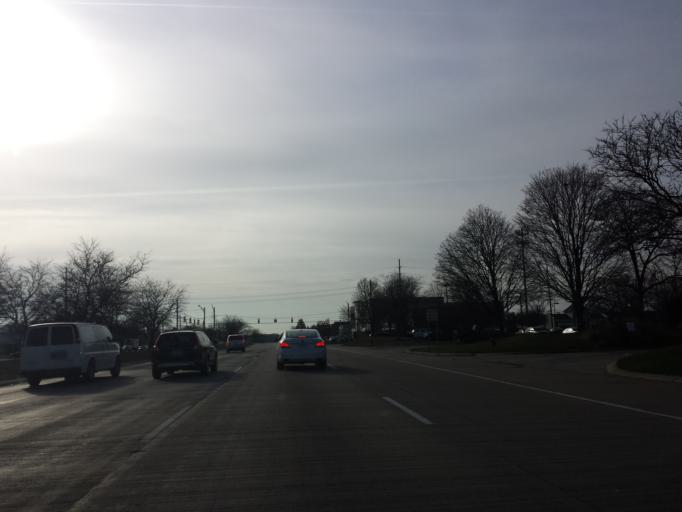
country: US
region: Michigan
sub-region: Oakland County
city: Bloomfield Hills
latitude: 42.5824
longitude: -83.2812
